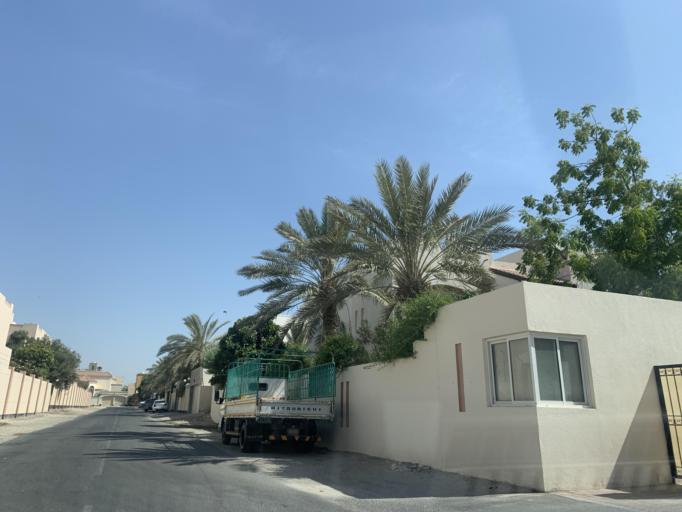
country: BH
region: Northern
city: Madinat `Isa
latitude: 26.1899
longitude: 50.4724
